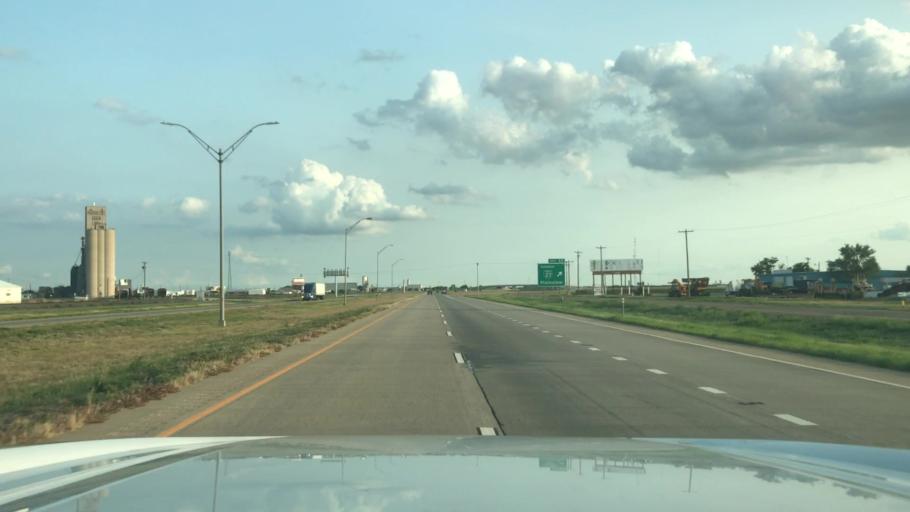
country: US
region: Texas
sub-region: Hale County
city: Seth Ward
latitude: 34.2441
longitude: -101.7089
